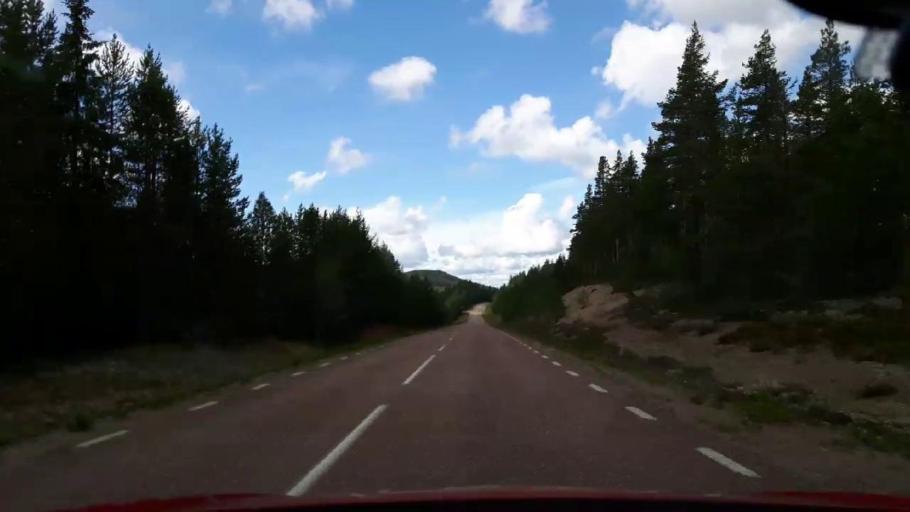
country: SE
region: Dalarna
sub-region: Alvdalens Kommun
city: AElvdalen
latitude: 61.7981
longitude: 13.6951
